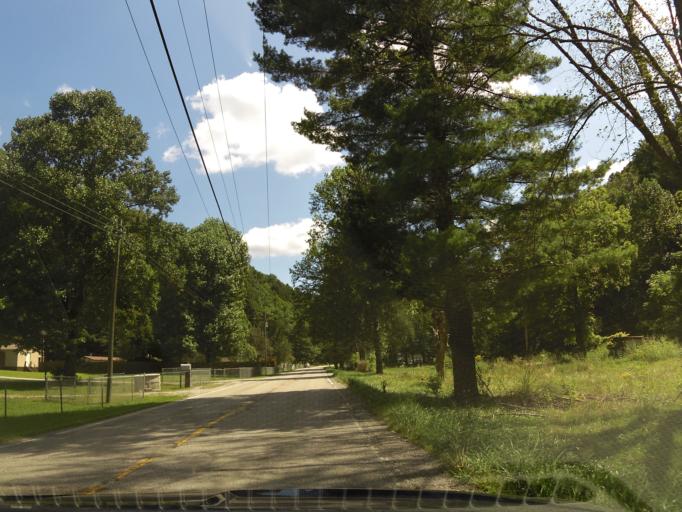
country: US
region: Kentucky
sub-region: Harlan County
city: Loyall
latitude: 36.9381
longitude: -83.3829
